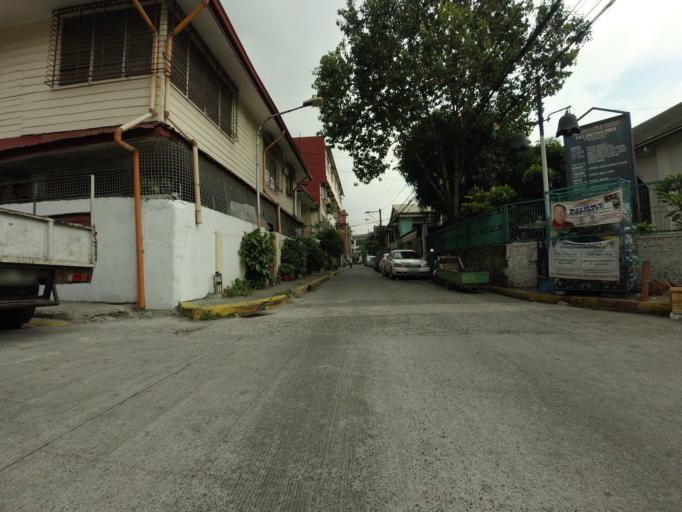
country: PH
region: Metro Manila
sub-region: City of Manila
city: Quiapo
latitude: 14.5781
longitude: 120.9959
